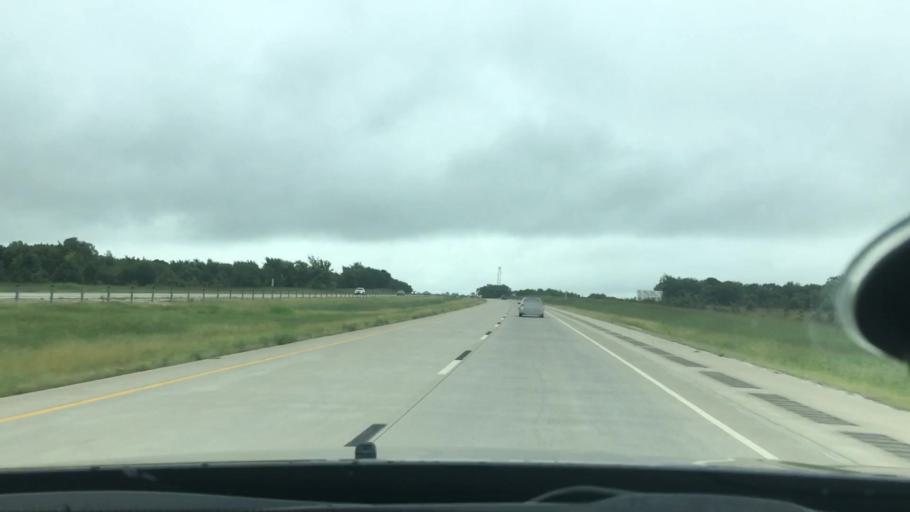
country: US
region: Oklahoma
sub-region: Okmulgee County
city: Henryetta
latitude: 35.4274
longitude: -96.0664
